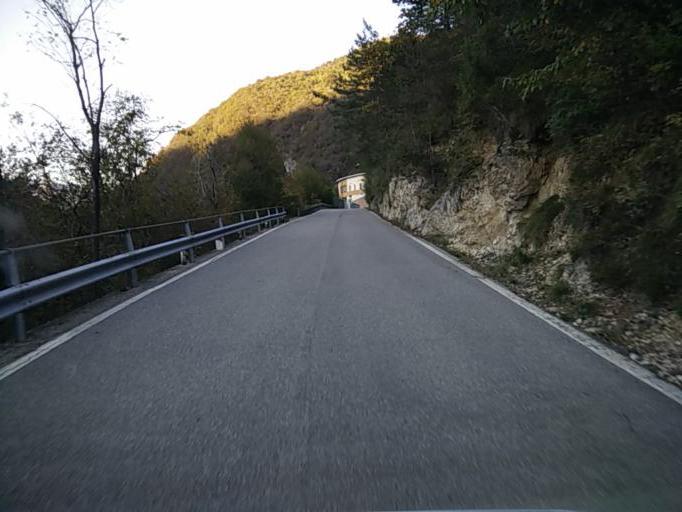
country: IT
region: Lombardy
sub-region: Provincia di Brescia
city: Gargnano
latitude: 45.7068
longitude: 10.6138
